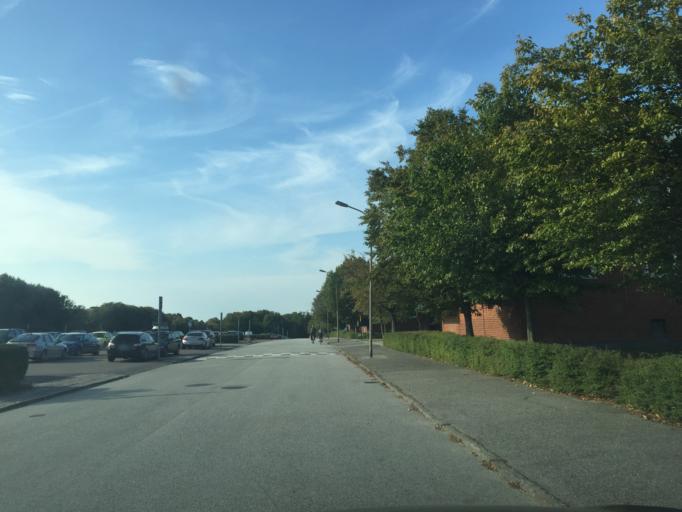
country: SE
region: Skane
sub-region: Lunds Kommun
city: Lund
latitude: 55.7109
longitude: 13.1684
